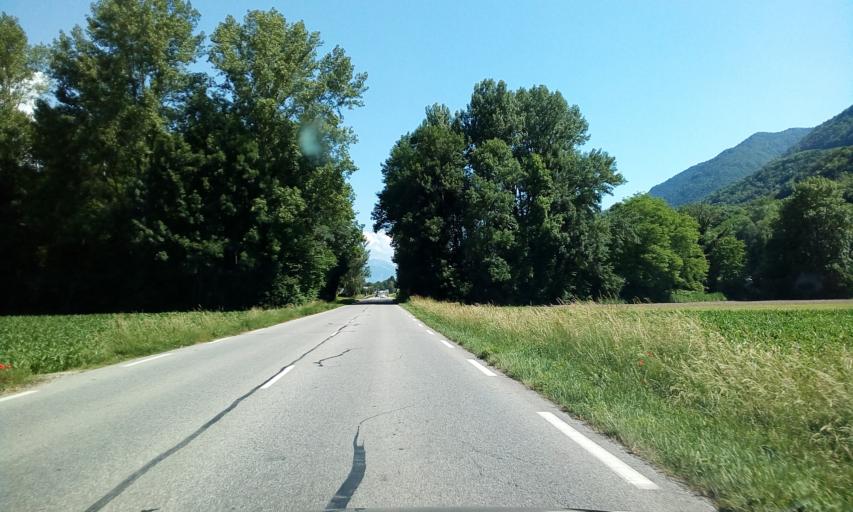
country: FR
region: Rhone-Alpes
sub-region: Departement de l'Isere
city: Tencin
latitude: 45.3219
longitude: 5.9670
